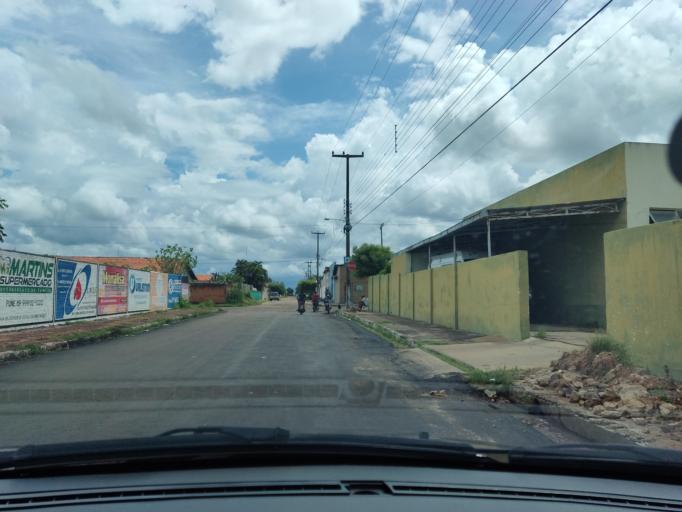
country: BR
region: Piaui
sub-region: Valenca Do Piaui
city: Valenca do Piaui
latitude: -6.4004
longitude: -41.7379
